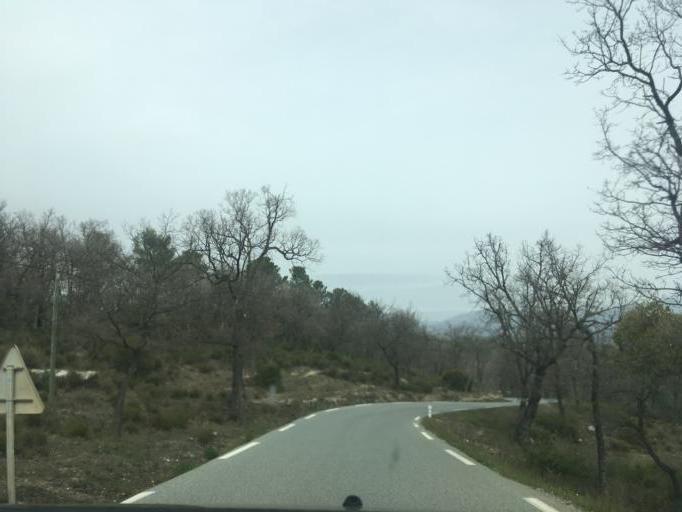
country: FR
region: Provence-Alpes-Cote d'Azur
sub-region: Departement du Var
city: Saint-Paul-en-Foret
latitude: 43.5778
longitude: 6.7266
